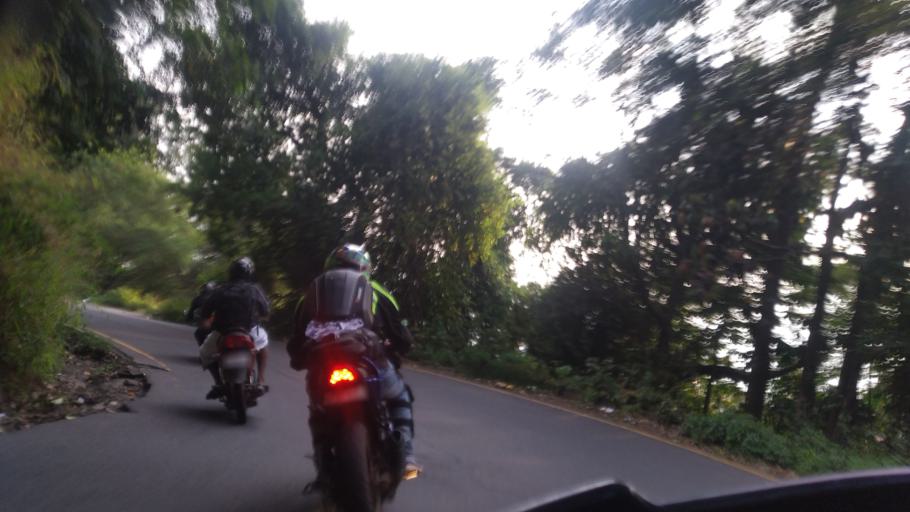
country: IN
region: Kerala
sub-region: Wayanad
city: Kalpetta
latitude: 11.5142
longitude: 76.0153
